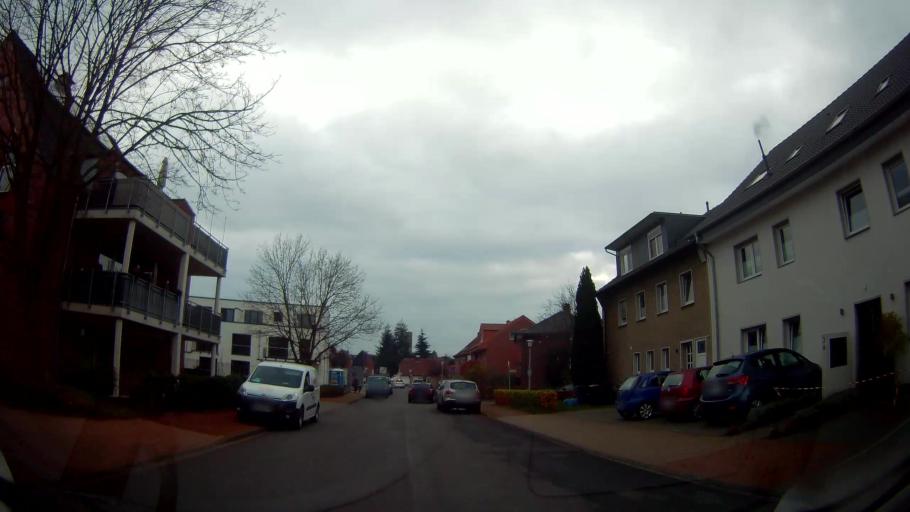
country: DE
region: North Rhine-Westphalia
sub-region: Regierungsbezirk Munster
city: Haltern
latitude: 51.7472
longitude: 7.1888
